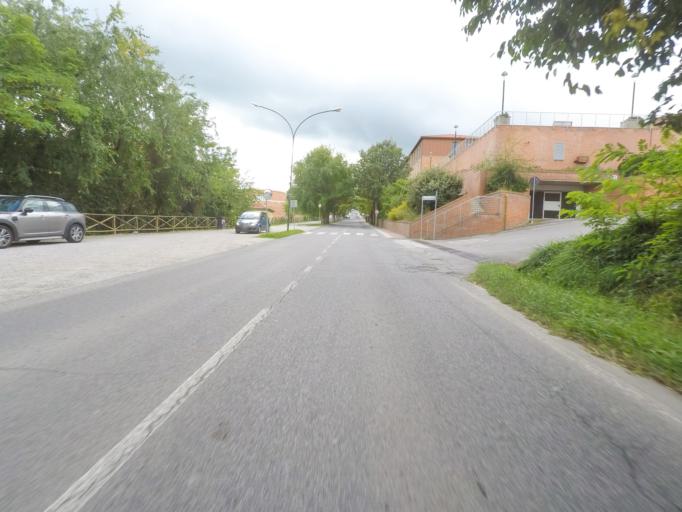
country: IT
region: Tuscany
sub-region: Provincia di Siena
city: Montepulciano
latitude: 43.1026
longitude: 11.7857
